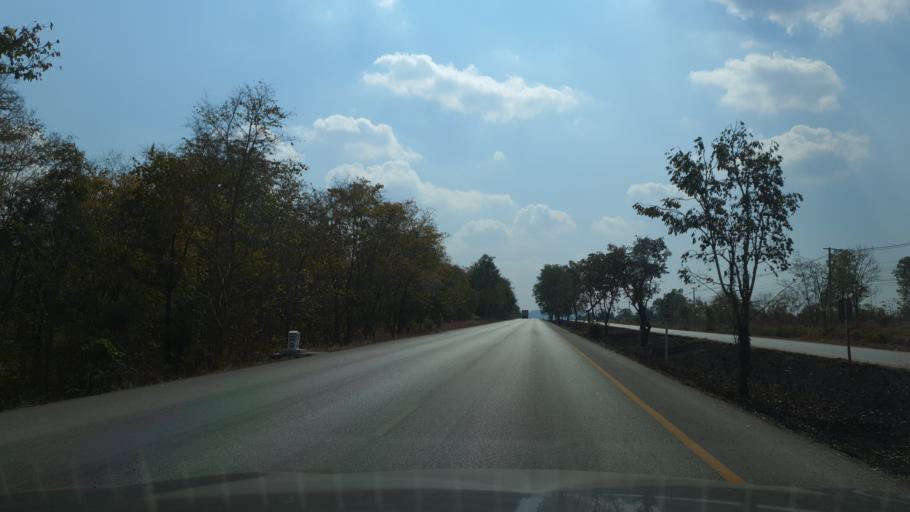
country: TH
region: Lampang
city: Mae Phrik
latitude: 17.3904
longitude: 99.1488
